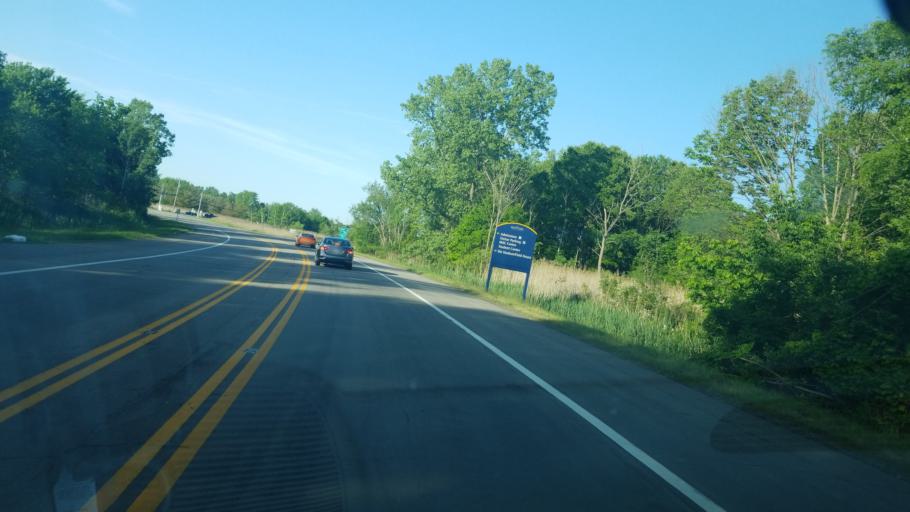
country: US
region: Ohio
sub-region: Portage County
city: Kent
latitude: 41.1365
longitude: -81.3226
